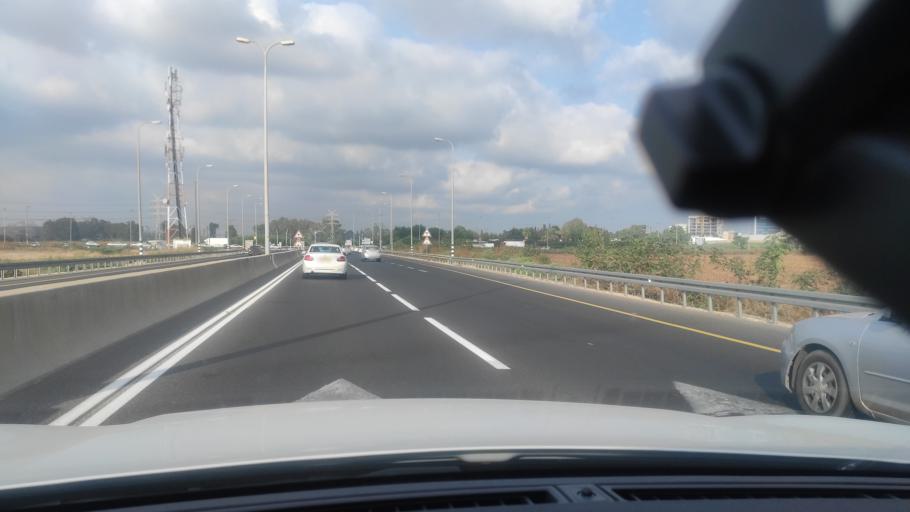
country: IL
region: Central District
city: Hod HaSharon
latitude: 32.1307
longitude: 34.9046
